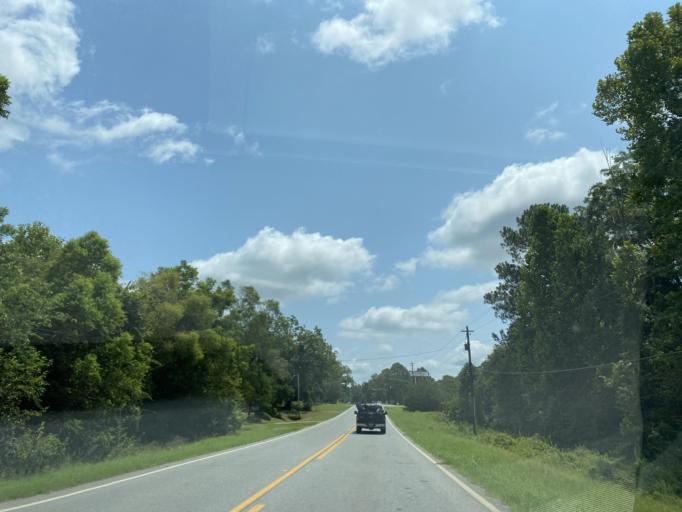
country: US
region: Georgia
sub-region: Telfair County
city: Helena
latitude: 32.0173
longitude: -83.0601
